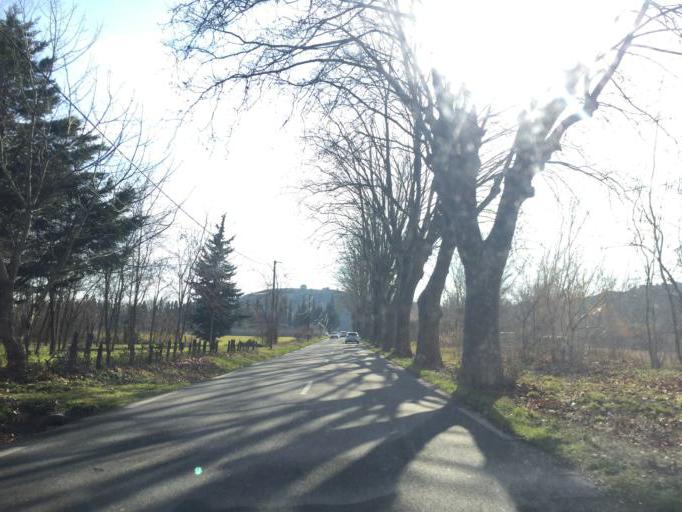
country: FR
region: Languedoc-Roussillon
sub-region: Departement du Gard
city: Roquemaure
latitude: 44.0388
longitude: 4.7888
